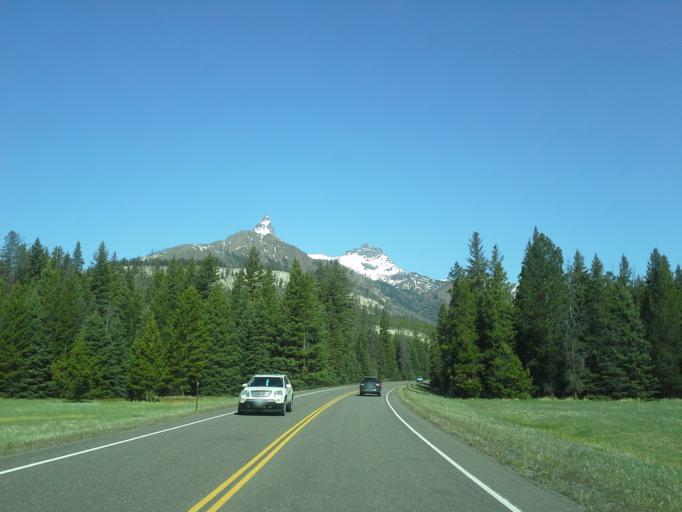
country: US
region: Montana
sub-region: Carbon County
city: Red Lodge
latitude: 44.9583
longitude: -109.8135
